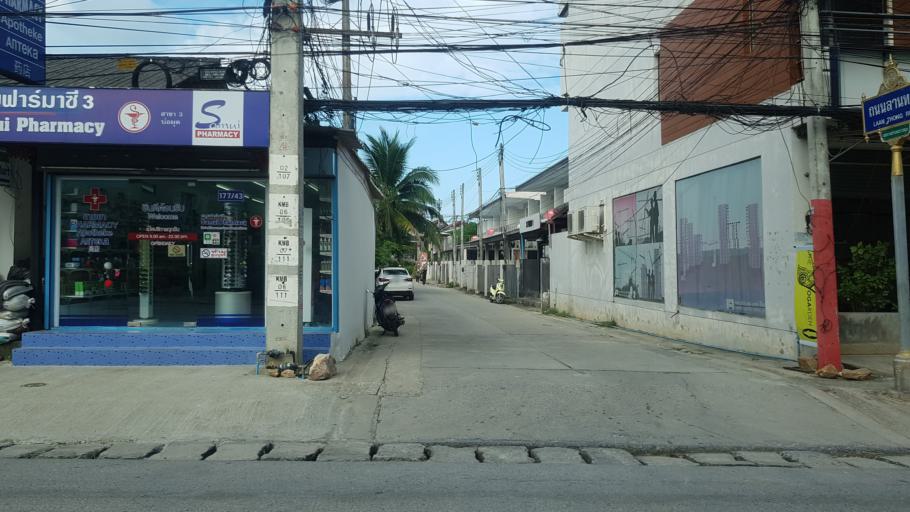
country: TH
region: Surat Thani
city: Ko Samui
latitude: 9.5577
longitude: 100.0281
